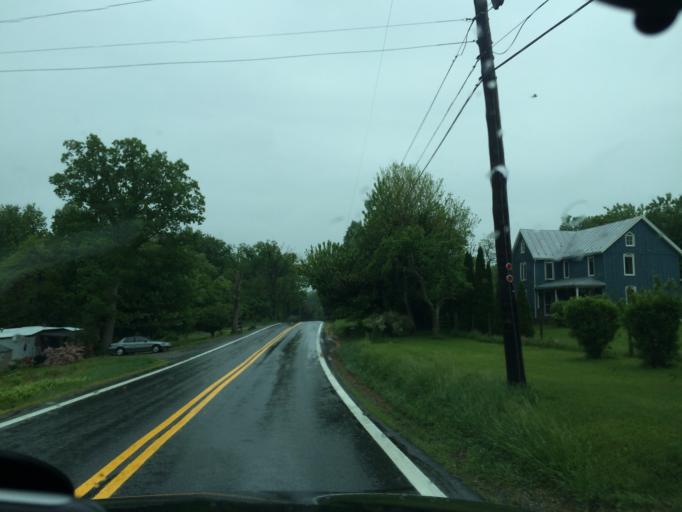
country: US
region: Maryland
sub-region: Washington County
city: Highfield-Cascade
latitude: 39.6899
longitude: -77.4915
